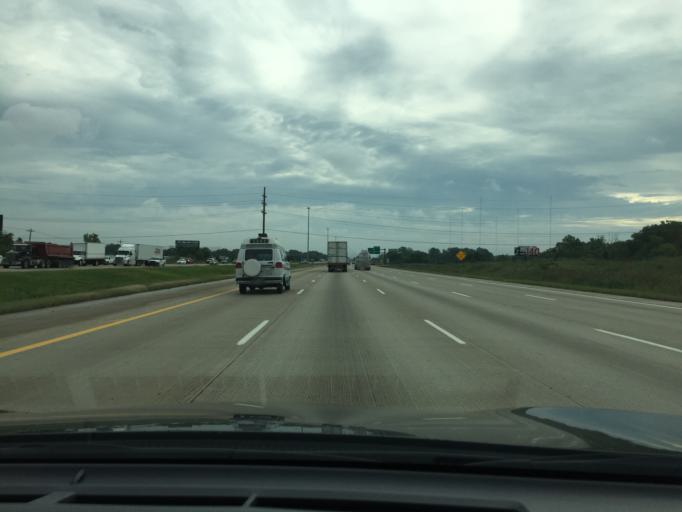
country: US
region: Michigan
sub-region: Wayne County
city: Taylor
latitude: 42.2651
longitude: -83.2622
